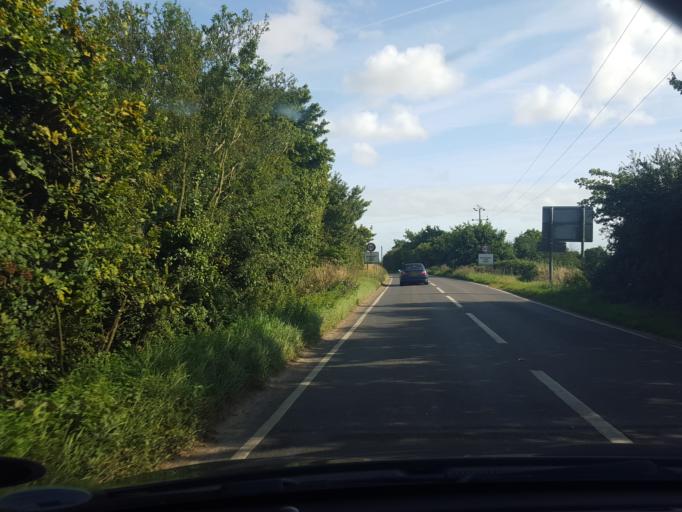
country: GB
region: England
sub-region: Essex
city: Little Clacton
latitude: 51.8848
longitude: 1.1629
